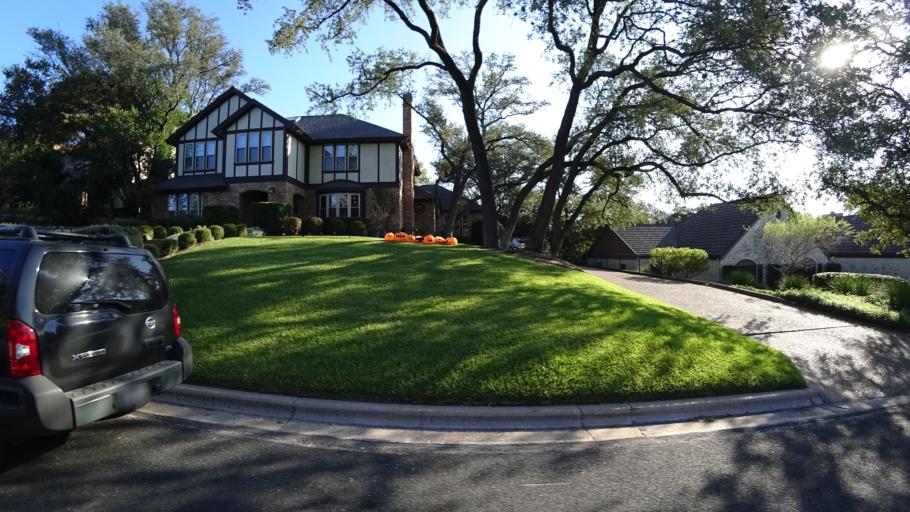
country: US
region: Texas
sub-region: Travis County
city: Rollingwood
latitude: 30.2622
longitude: -97.7994
